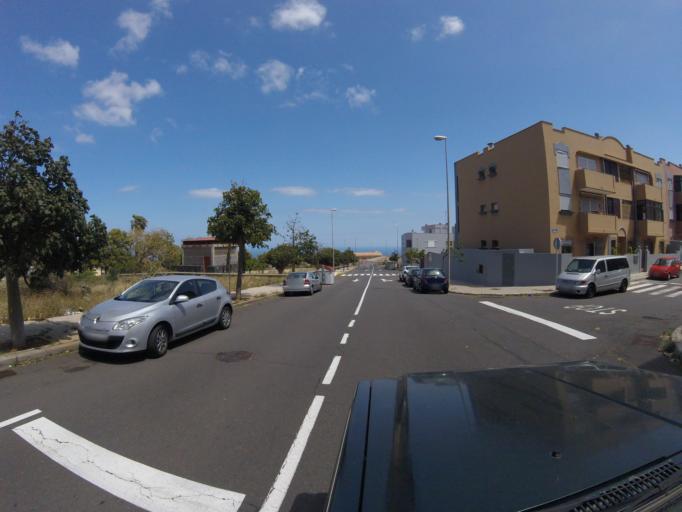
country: ES
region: Canary Islands
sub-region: Provincia de Santa Cruz de Tenerife
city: La Laguna
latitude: 28.4452
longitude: -16.3134
